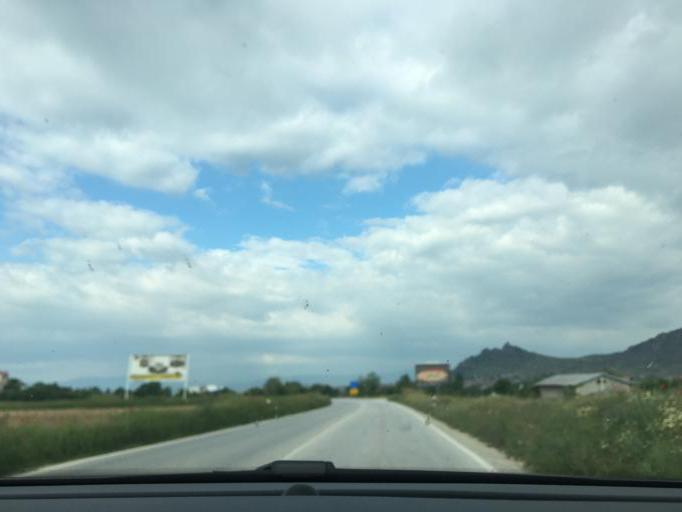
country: MK
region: Prilep
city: Prilep
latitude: 41.3591
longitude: 21.5877
